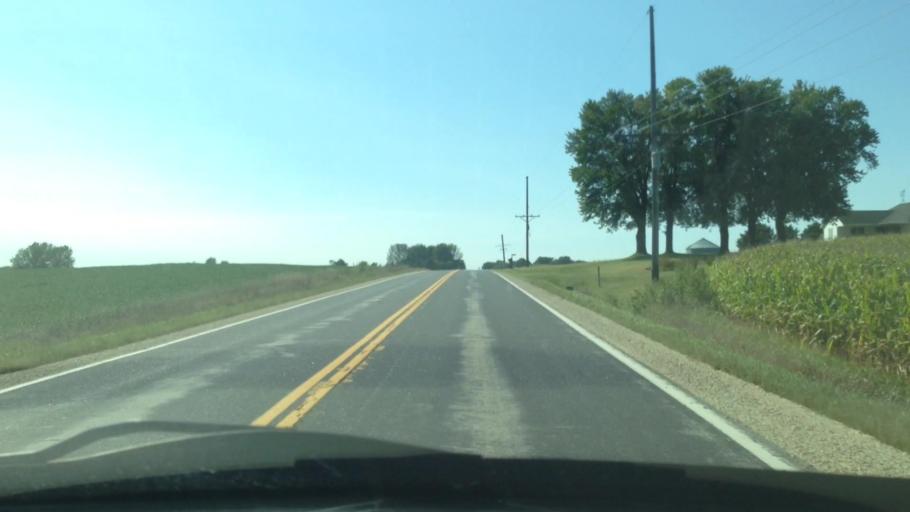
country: US
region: Minnesota
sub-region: Winona County
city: Lewiston
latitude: 43.9404
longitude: -91.7765
